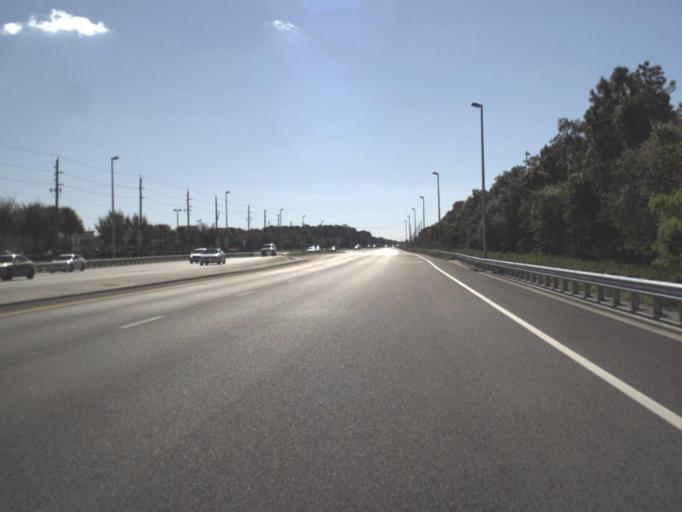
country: US
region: Florida
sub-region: Lee County
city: Gateway
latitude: 26.6174
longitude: -81.7666
